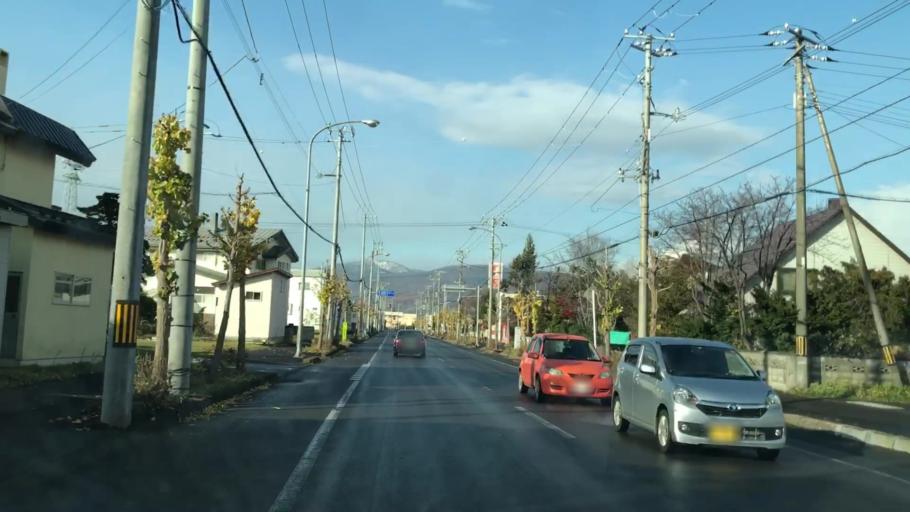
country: JP
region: Hokkaido
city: Yoichi
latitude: 43.1828
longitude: 140.8037
